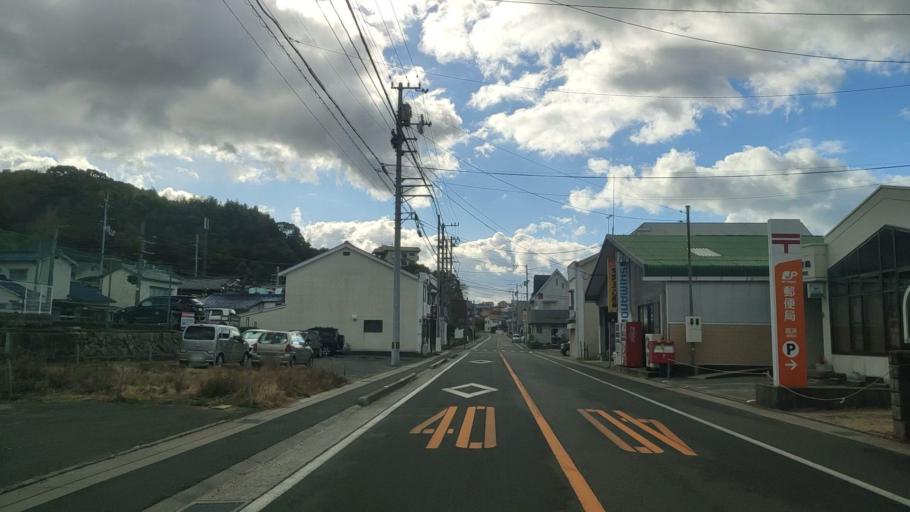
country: JP
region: Ehime
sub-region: Shikoku-chuo Shi
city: Matsuyama
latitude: 33.8831
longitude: 132.7018
